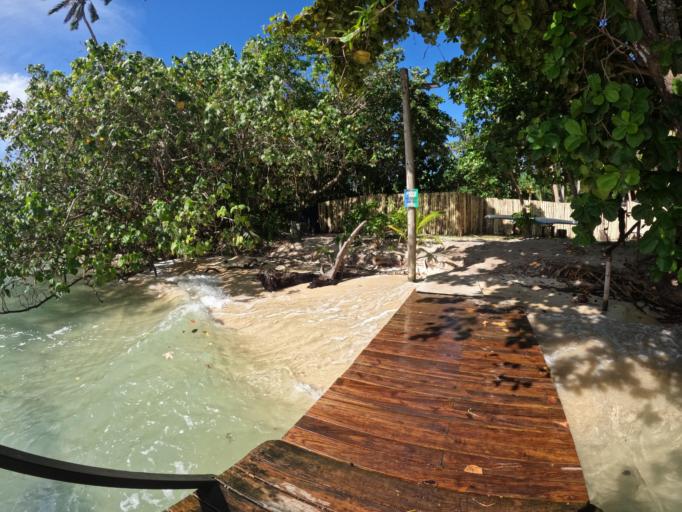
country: FJ
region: Central
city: Suva
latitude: -17.8096
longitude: 178.7216
